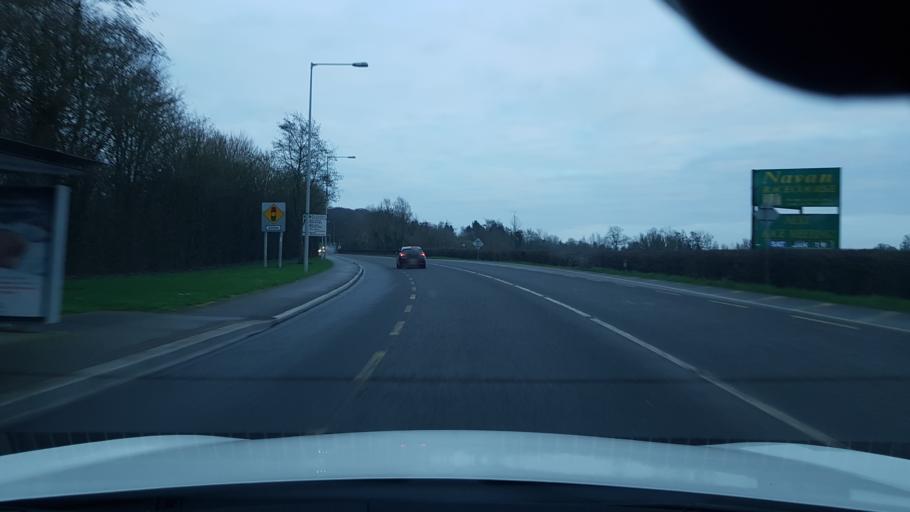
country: IE
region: Leinster
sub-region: An Mhi
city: Navan
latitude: 53.6322
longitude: -6.6638
